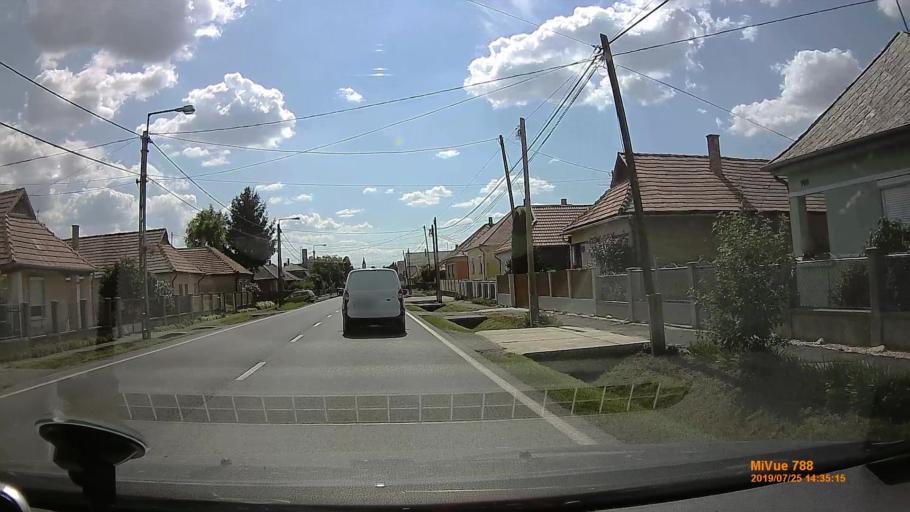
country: HU
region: Borsod-Abauj-Zemplen
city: Encs
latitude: 48.3271
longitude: 21.0925
